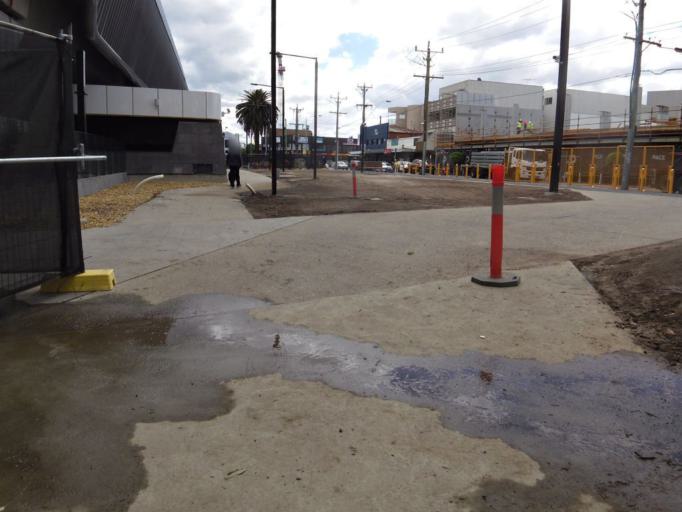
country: AU
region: Victoria
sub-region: Glen Eira
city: Carnegie
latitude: -37.8861
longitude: 145.0588
